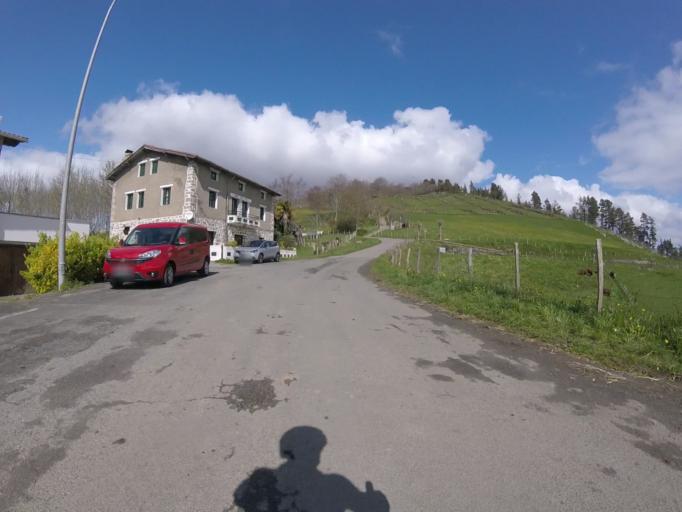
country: ES
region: Basque Country
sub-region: Provincia de Guipuzcoa
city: Albiztur
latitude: 43.1350
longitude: -2.1082
